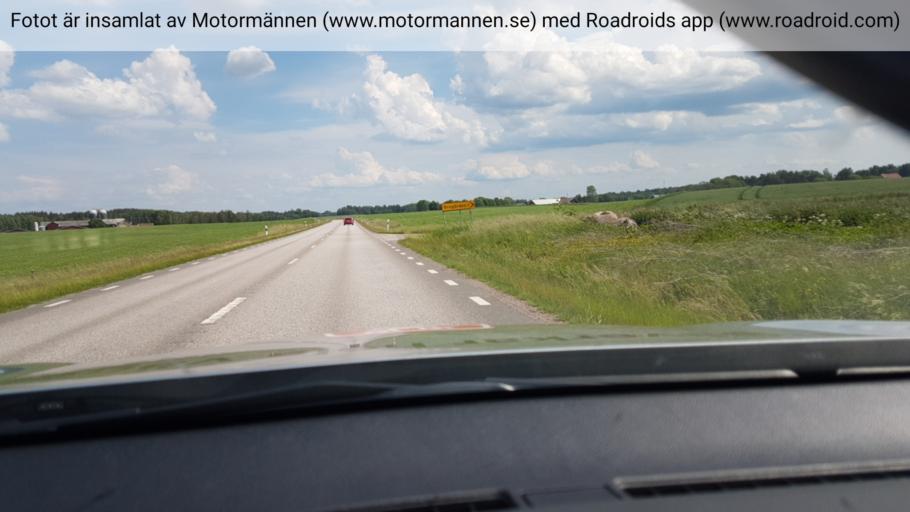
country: SE
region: Vaestra Goetaland
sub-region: Tibro Kommun
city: Tibro
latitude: 58.3507
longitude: 14.0859
